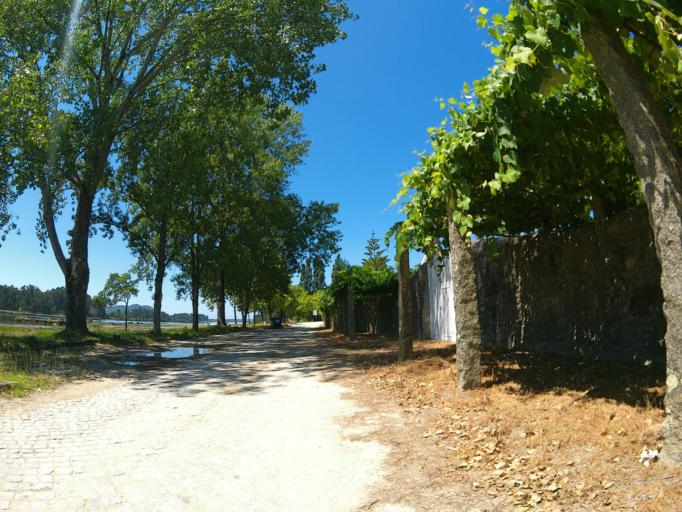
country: PT
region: Viana do Castelo
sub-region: Viana do Castelo
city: Darque
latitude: 41.7014
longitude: -8.7477
